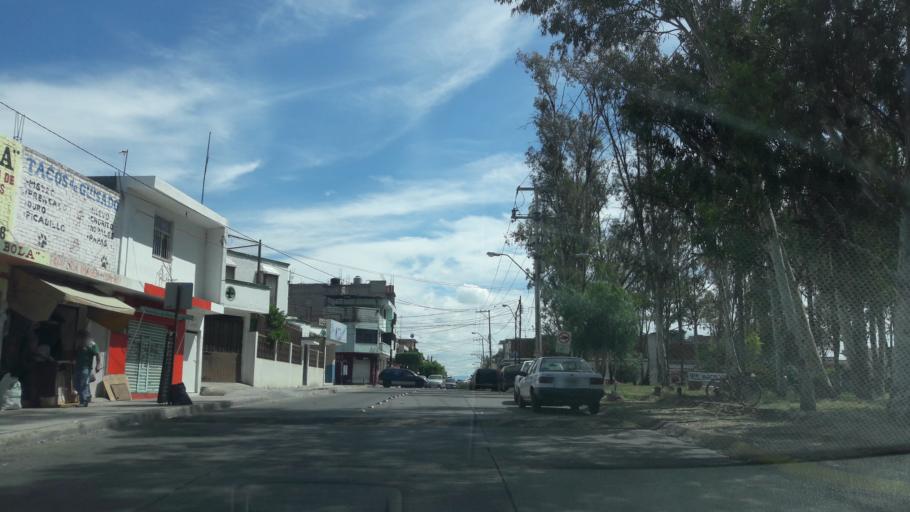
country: MX
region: Guanajuato
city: Leon
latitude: 21.1098
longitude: -101.7001
